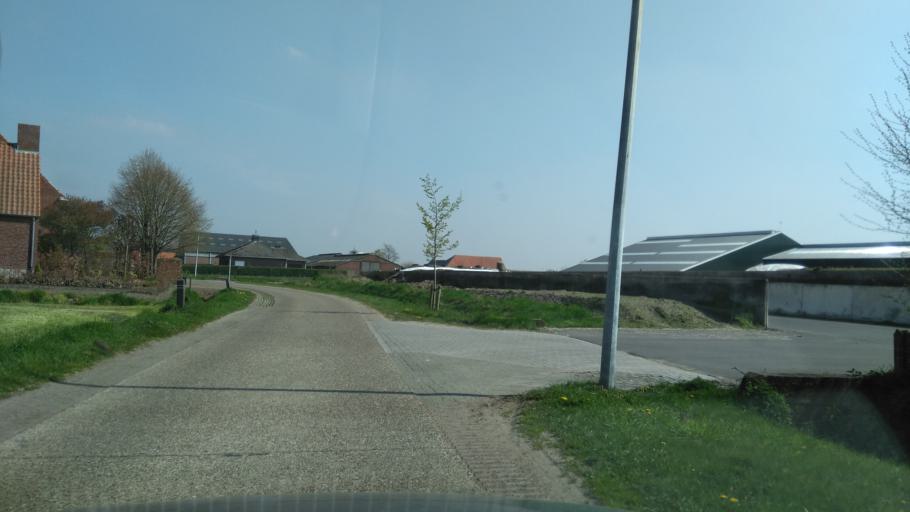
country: BE
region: Flanders
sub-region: Provincie Antwerpen
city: Baarle-Hertog
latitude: 51.4049
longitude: 4.9025
